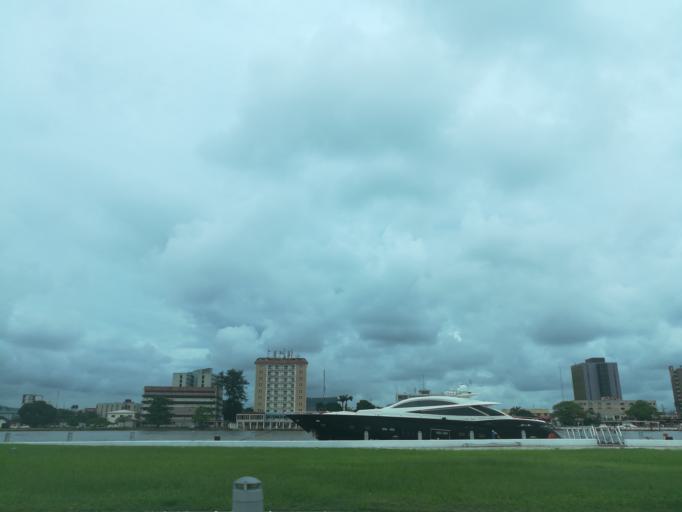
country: NG
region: Lagos
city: Lagos
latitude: 6.4407
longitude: 3.4084
